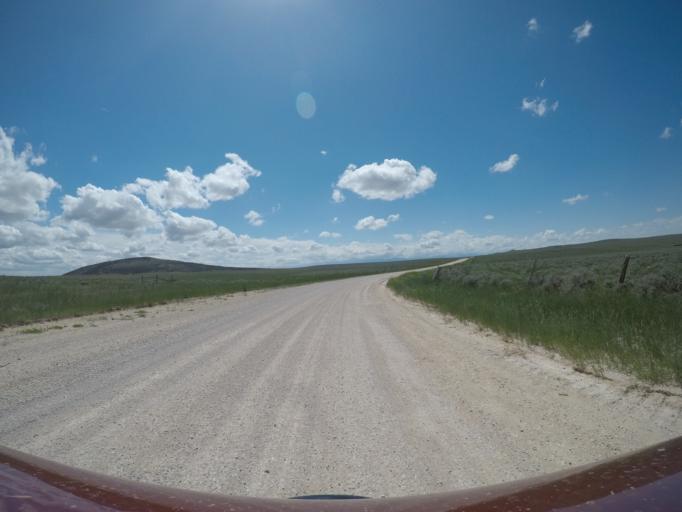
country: US
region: Wyoming
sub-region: Park County
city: Powell
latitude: 45.2052
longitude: -108.7321
